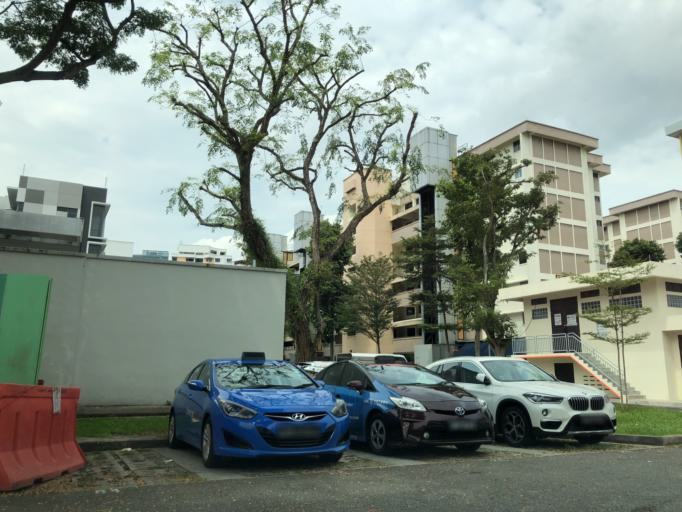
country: SG
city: Singapore
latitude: 1.3146
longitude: 103.8497
